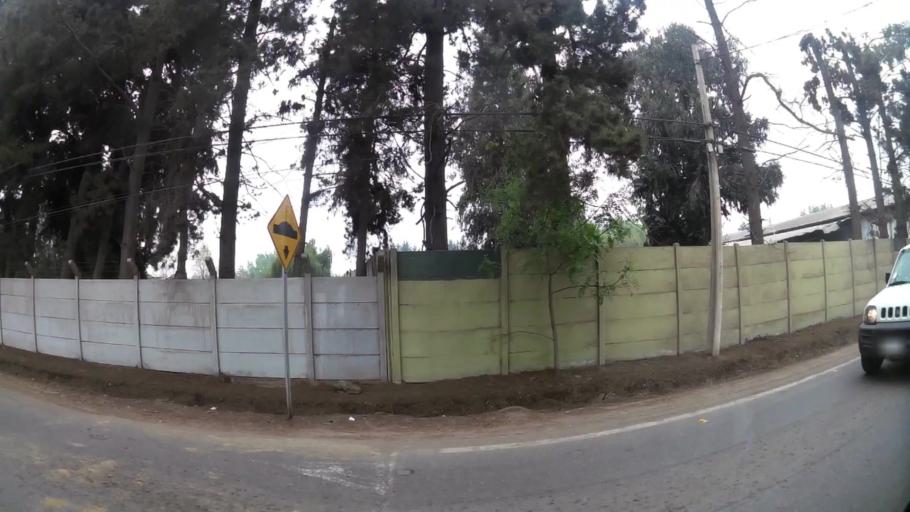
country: CL
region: Santiago Metropolitan
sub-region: Provincia de Chacabuco
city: Chicureo Abajo
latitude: -33.2466
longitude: -70.7251
